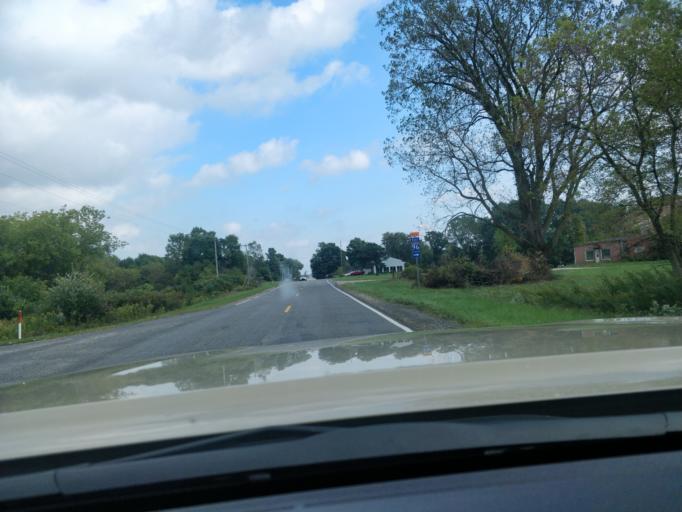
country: US
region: Michigan
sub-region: Ionia County
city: Saranac
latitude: 42.8862
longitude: -85.2448
